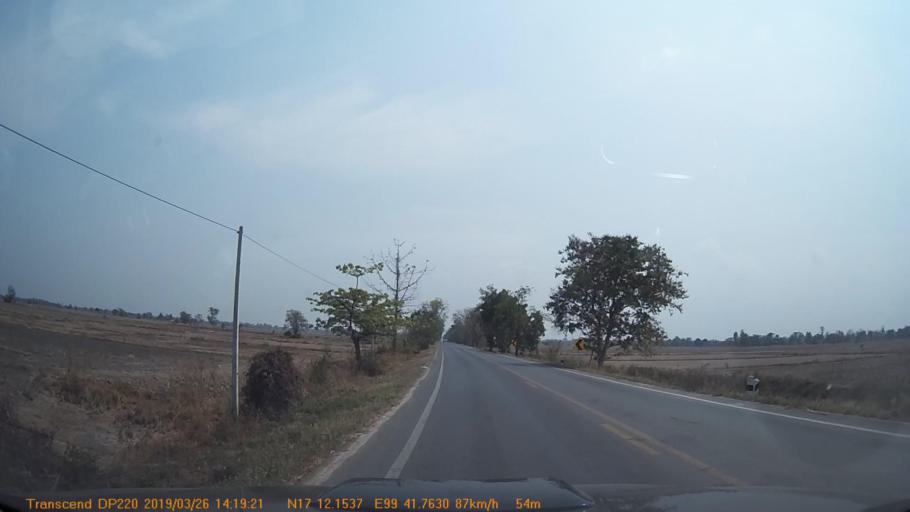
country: TH
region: Sukhothai
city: Si Samrong
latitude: 17.2022
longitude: 99.6961
